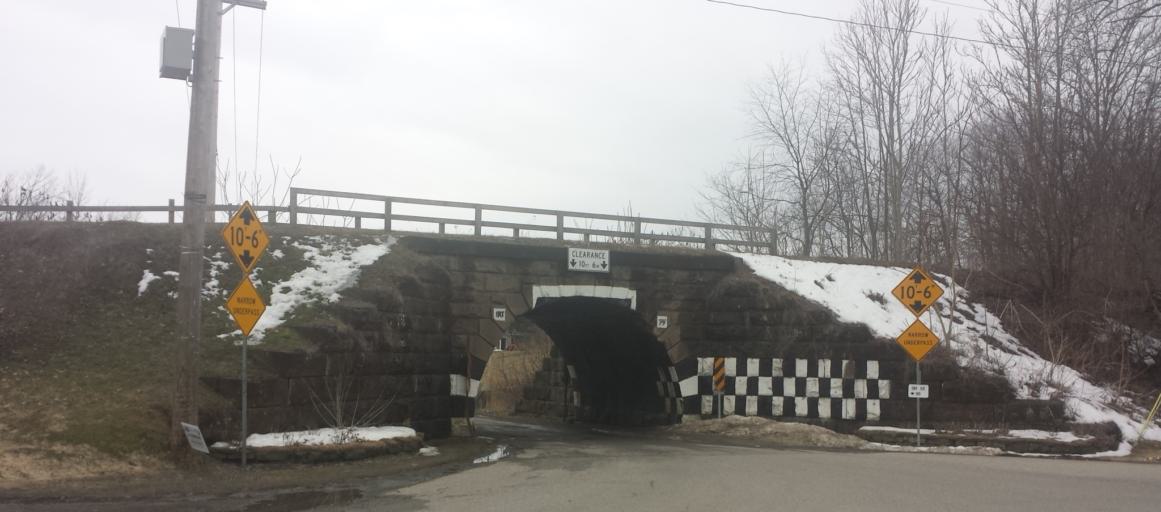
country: US
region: Pennsylvania
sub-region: Mercer County
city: Greenville
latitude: 41.4847
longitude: -80.4429
